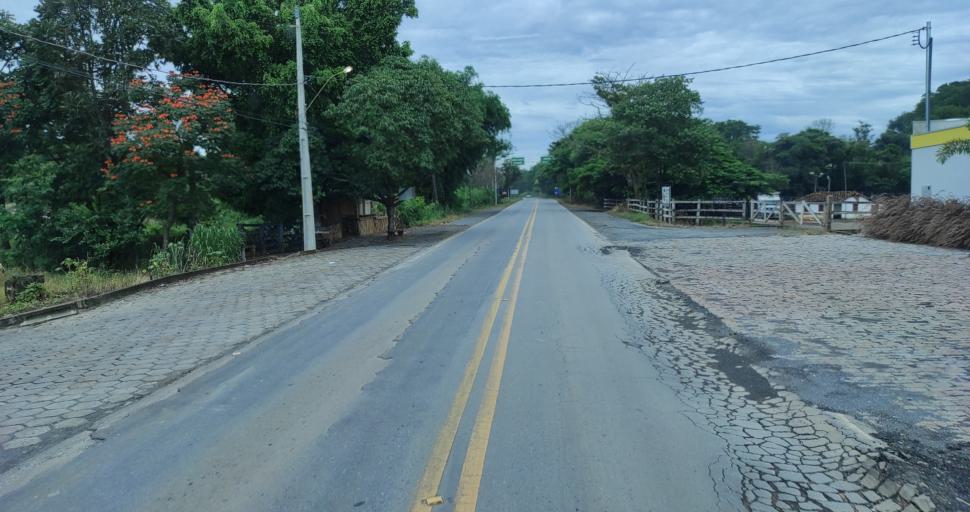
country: BR
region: Minas Gerais
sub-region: Arcos
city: Arcos
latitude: -20.3781
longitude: -45.6513
